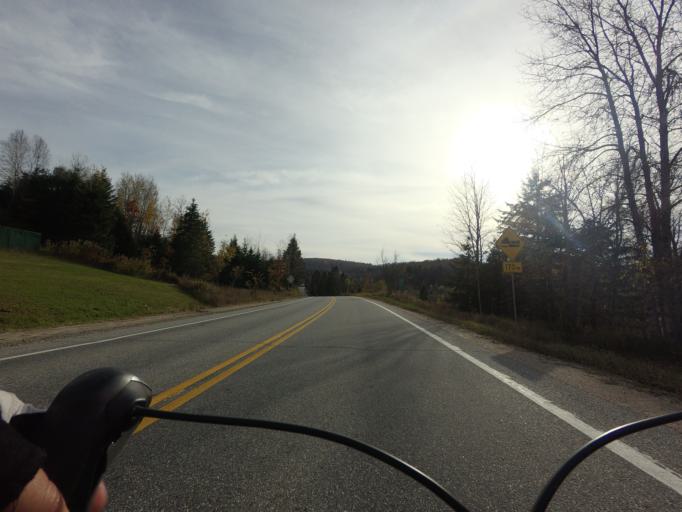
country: CA
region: Quebec
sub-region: Outaouais
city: Val-des-Monts
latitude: 45.6681
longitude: -75.7346
